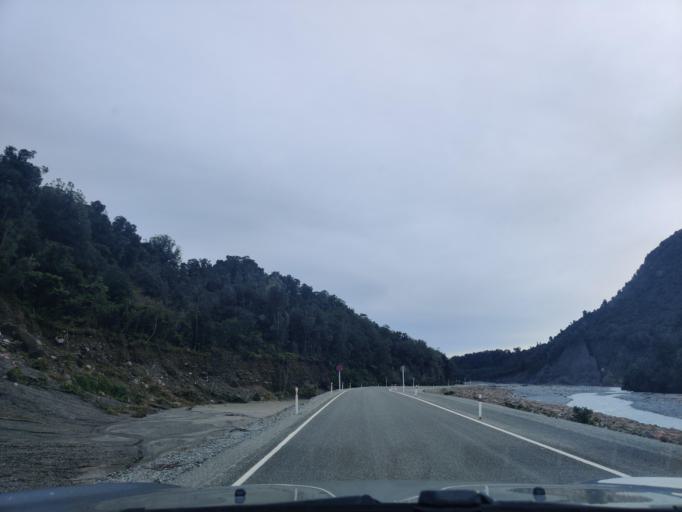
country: NZ
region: West Coast
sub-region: Westland District
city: Hokitika
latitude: -43.4046
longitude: 170.1781
